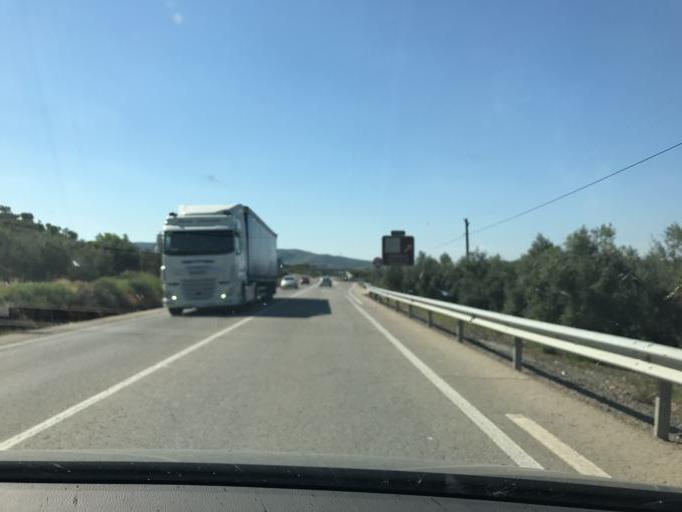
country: ES
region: Andalusia
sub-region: Province of Cordoba
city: Luque
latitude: 37.5751
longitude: -4.2682
